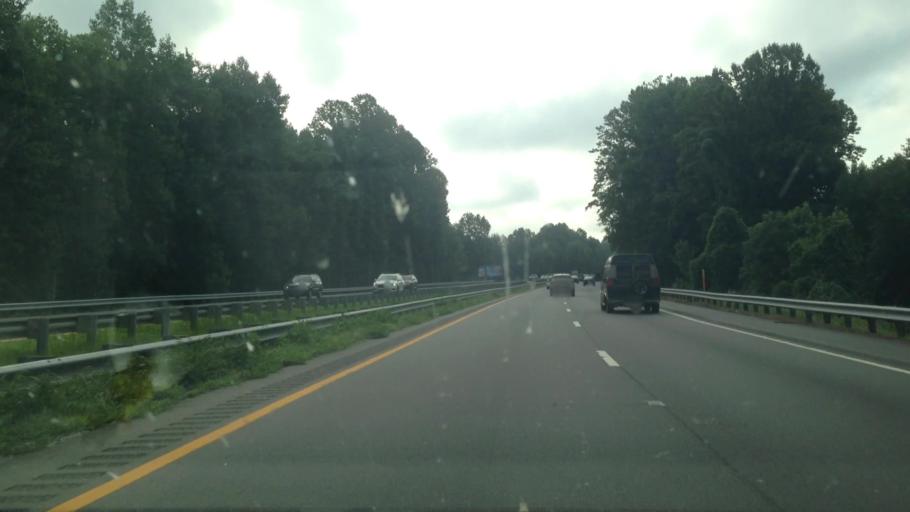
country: US
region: North Carolina
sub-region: Forsyth County
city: Kernersville
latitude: 36.1034
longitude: -80.0310
